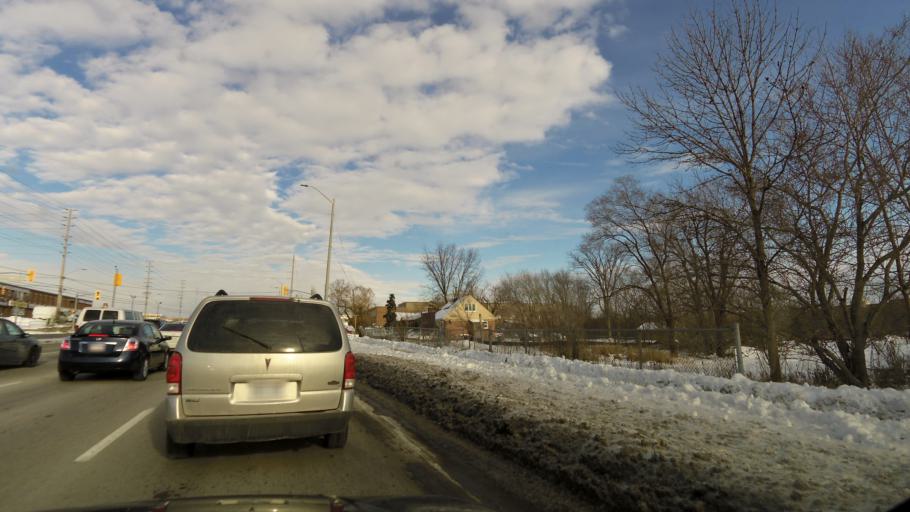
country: CA
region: Ontario
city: Mississauga
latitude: 43.6295
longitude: -79.6274
